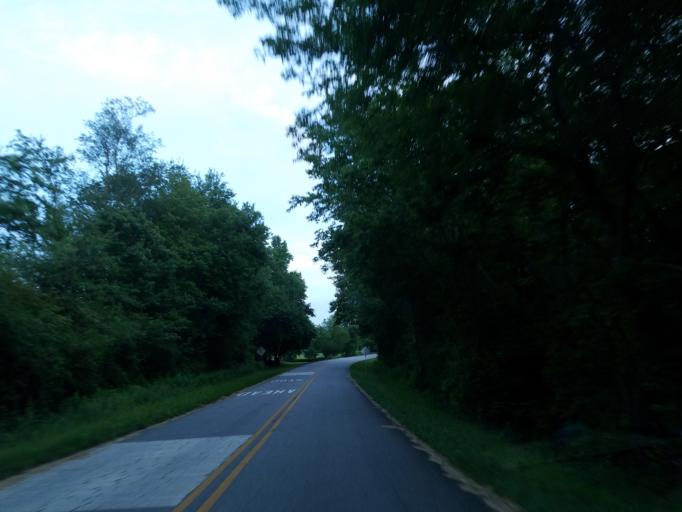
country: US
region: Georgia
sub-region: Dawson County
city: Dawsonville
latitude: 34.4859
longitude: -84.1713
